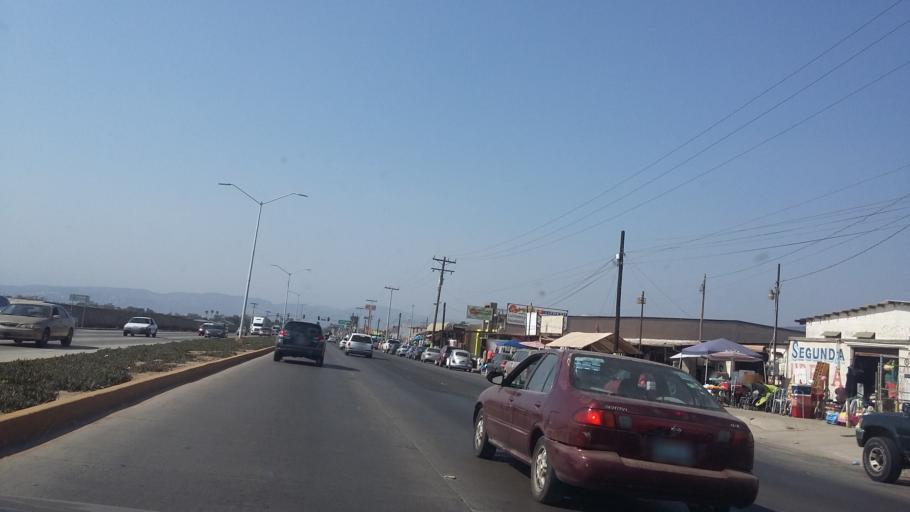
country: MX
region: Baja California
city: Rodolfo Sanchez Taboada
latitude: 31.7884
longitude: -116.5923
